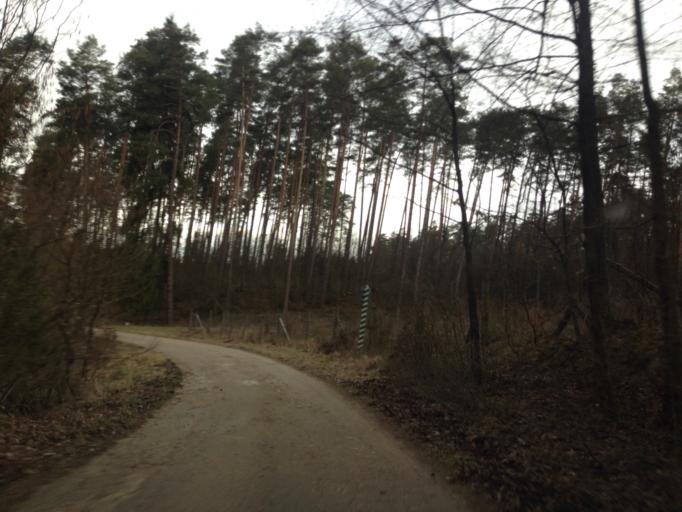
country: PL
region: Kujawsko-Pomorskie
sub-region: Powiat brodnicki
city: Gorzno
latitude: 53.1790
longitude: 19.6791
